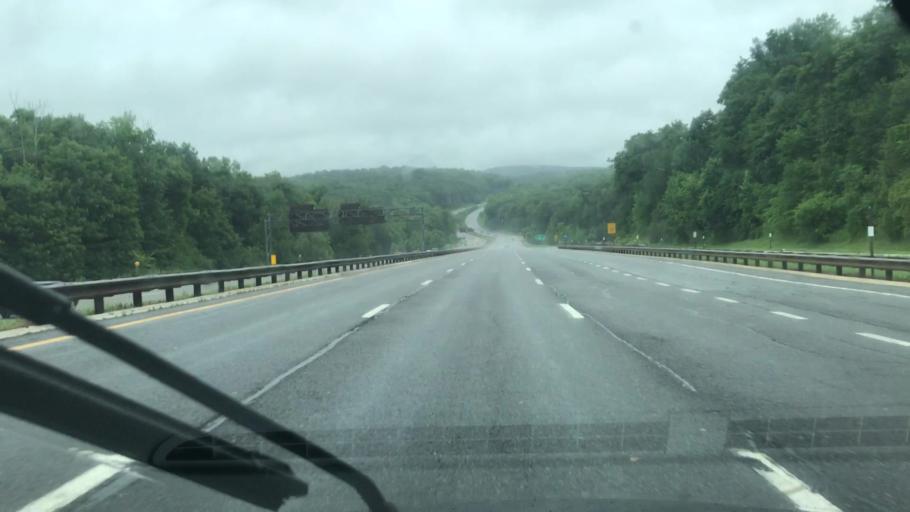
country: US
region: New York
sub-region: Westchester County
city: Jefferson Valley-Yorktown
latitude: 41.2944
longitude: -73.8221
